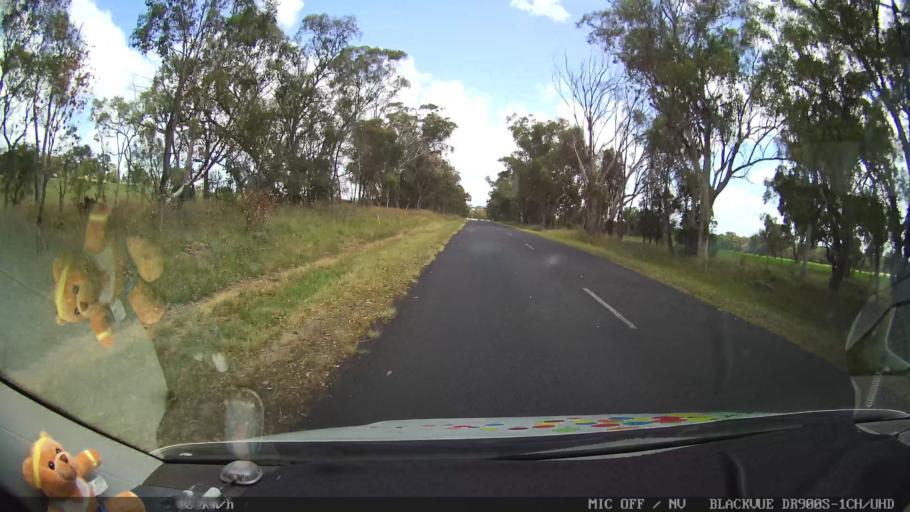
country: AU
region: New South Wales
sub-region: Glen Innes Severn
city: Glen Innes
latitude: -29.4792
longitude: 151.6827
